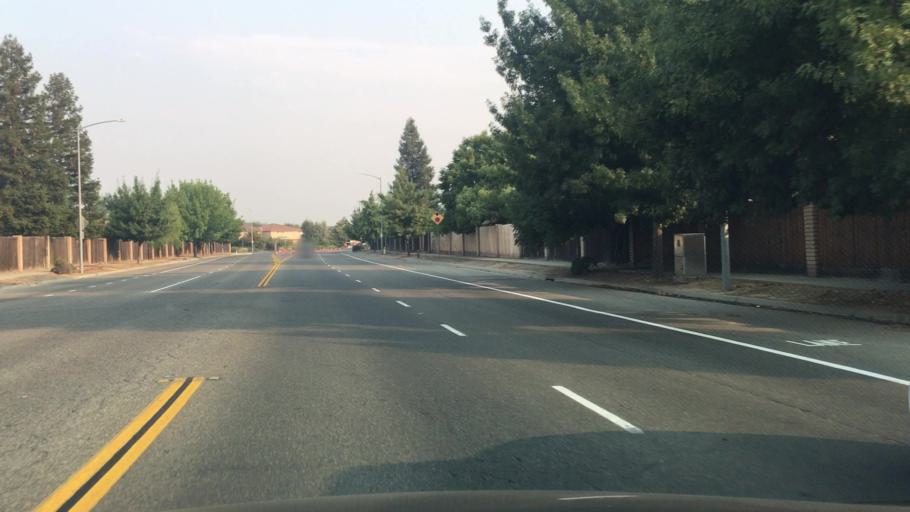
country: US
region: California
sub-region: Fresno County
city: Clovis
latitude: 36.8348
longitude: -119.6735
